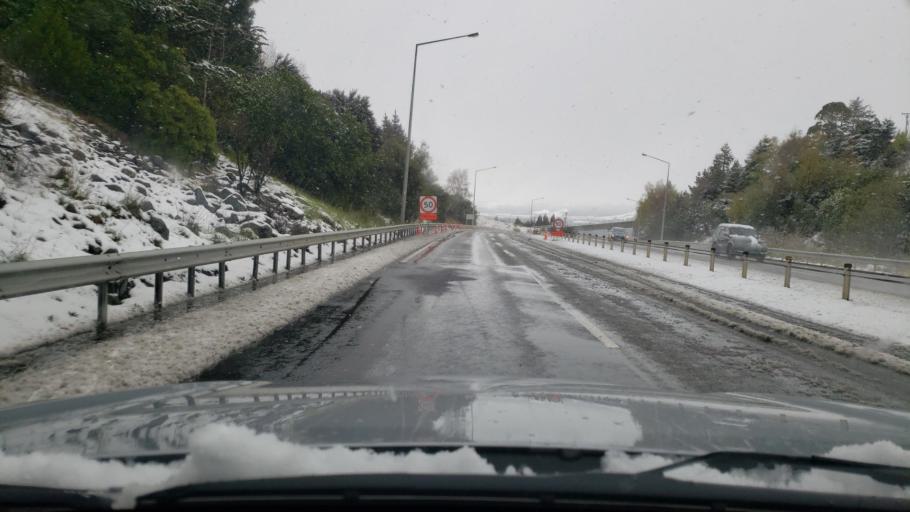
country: NZ
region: Otago
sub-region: Dunedin City
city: Dunedin
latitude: -45.8988
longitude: 170.3682
